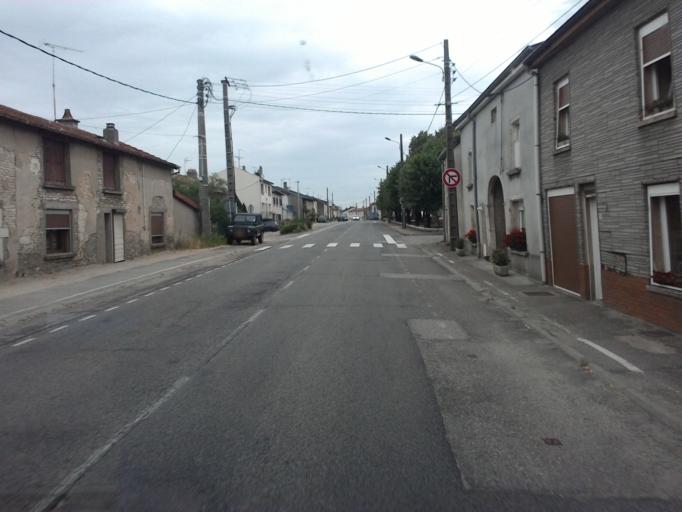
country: FR
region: Lorraine
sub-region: Departement de Meurthe-et-Moselle
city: Colombey-les-Belles
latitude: 48.5237
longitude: 5.8945
